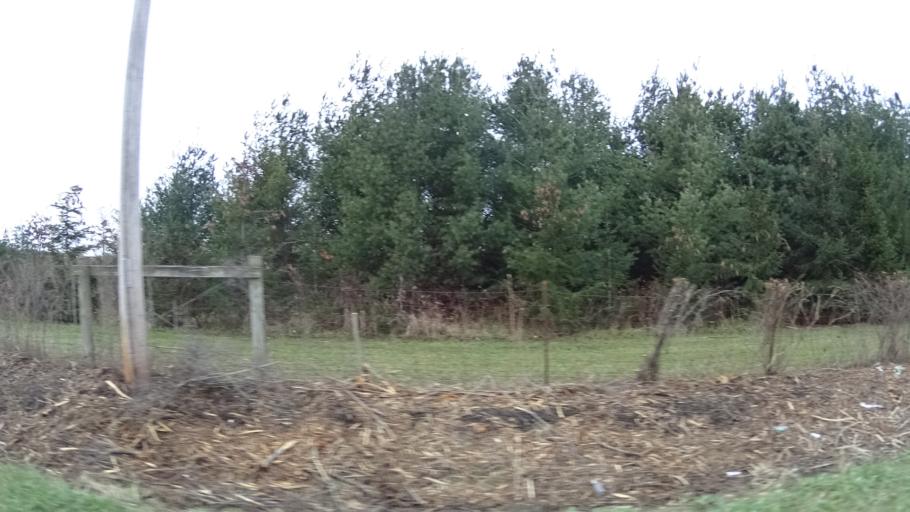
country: US
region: Ohio
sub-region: Lorain County
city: Wellington
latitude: 41.1415
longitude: -82.2692
